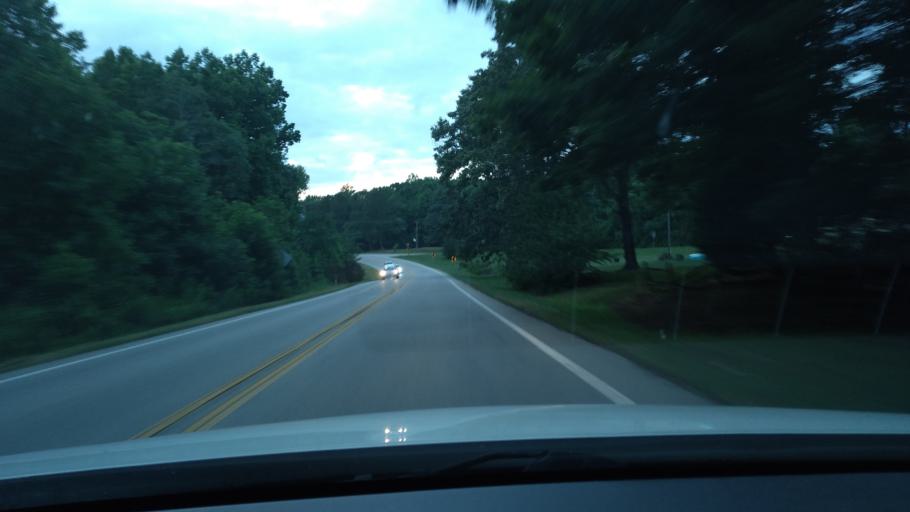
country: US
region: North Carolina
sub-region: Rockingham County
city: Reidsville
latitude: 36.3917
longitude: -79.5636
